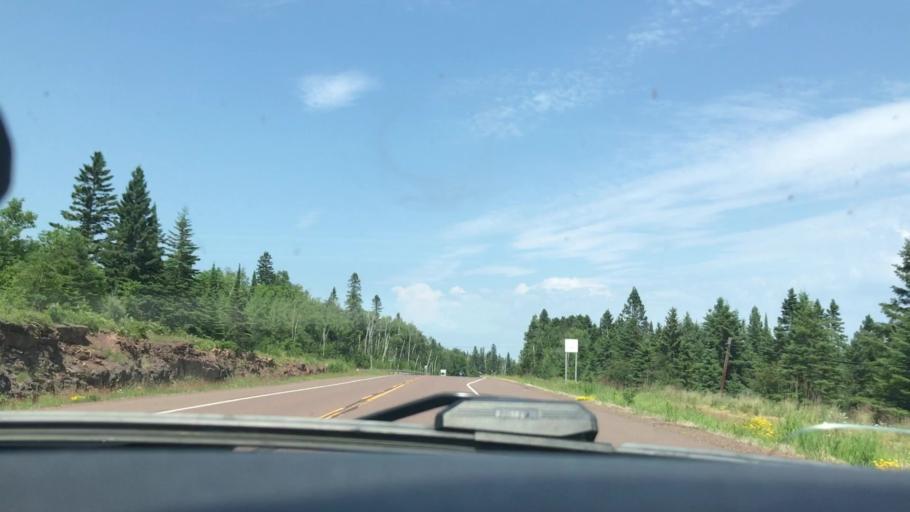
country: US
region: Minnesota
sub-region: Cook County
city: Grand Marais
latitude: 47.6172
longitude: -90.7551
